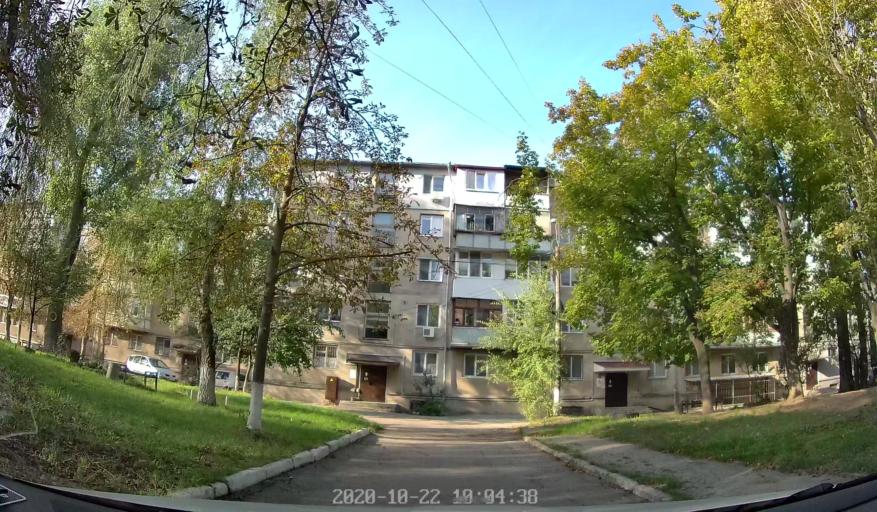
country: MD
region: Chisinau
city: Singera
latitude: 46.9401
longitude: 28.9253
